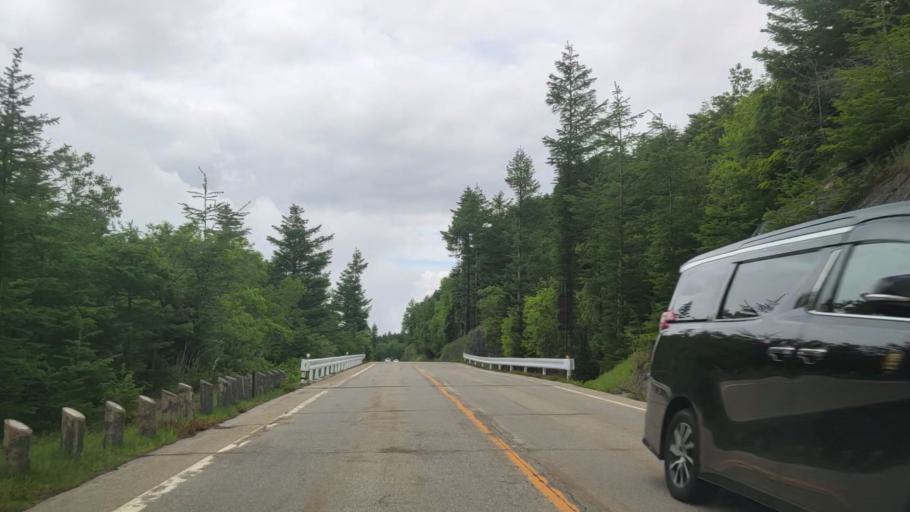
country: JP
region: Yamanashi
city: Fujikawaguchiko
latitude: 35.3845
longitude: 138.6908
